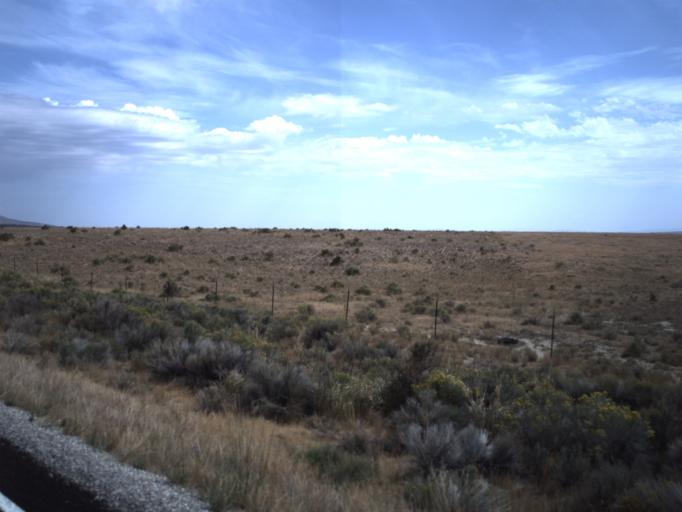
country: US
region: Idaho
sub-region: Cassia County
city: Burley
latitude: 41.7756
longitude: -113.4942
